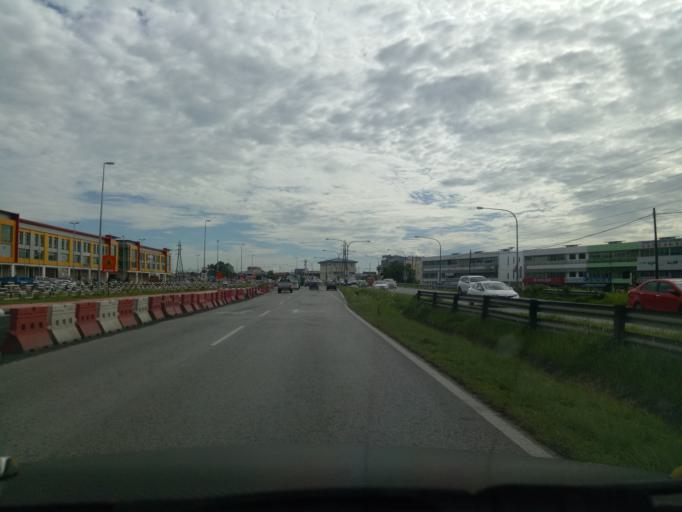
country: MY
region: Sarawak
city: Kuching
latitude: 1.4653
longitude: 110.3279
